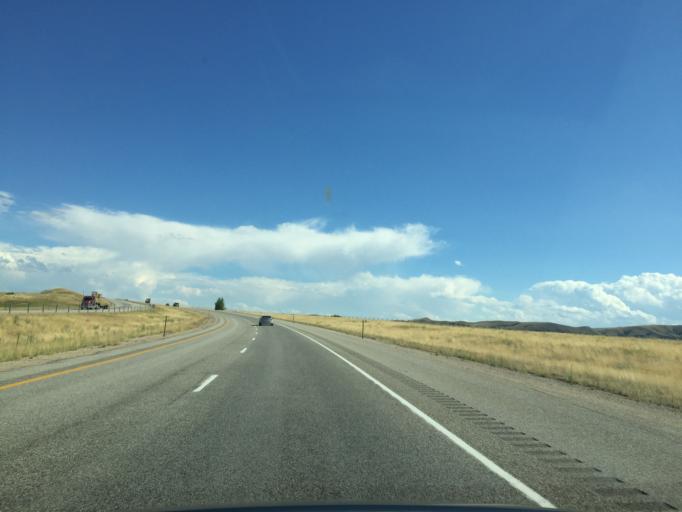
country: US
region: Wyoming
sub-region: Sheridan County
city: Sheridan
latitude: 44.6031
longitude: -106.8475
